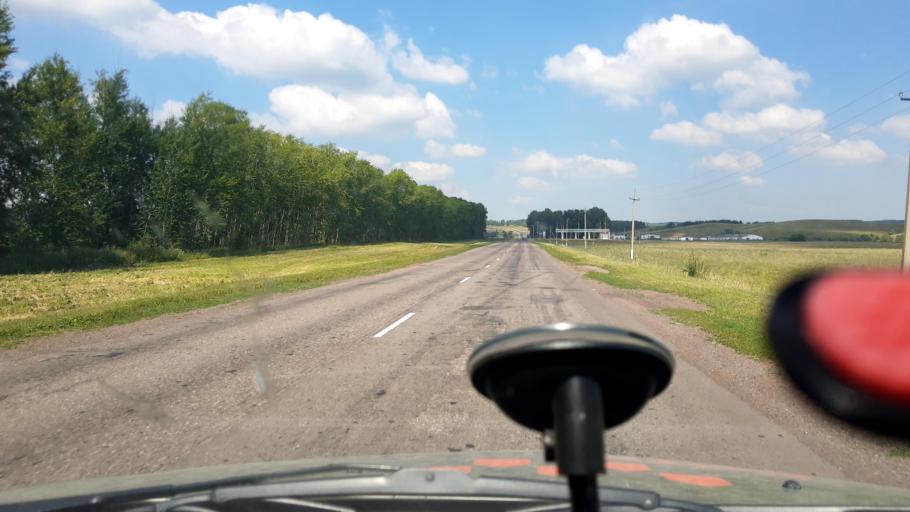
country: RU
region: Bashkortostan
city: Chekmagush
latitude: 54.8934
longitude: 54.5805
